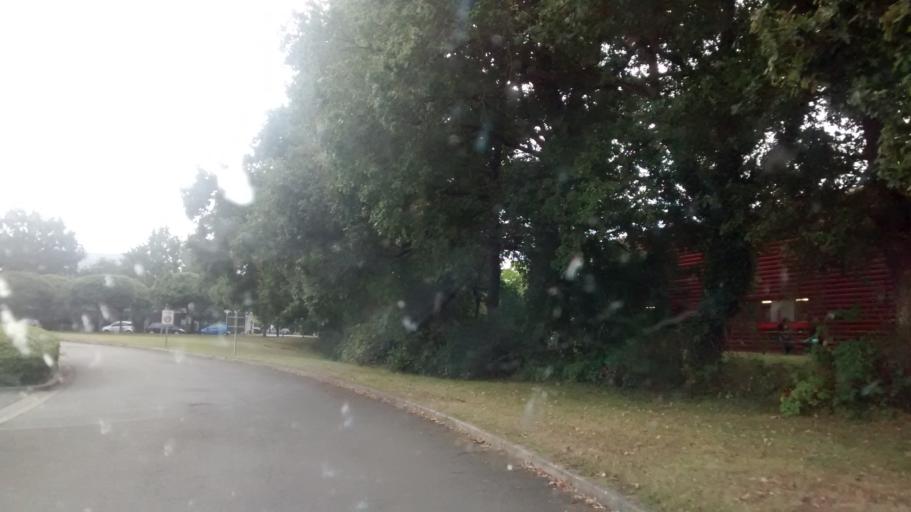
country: FR
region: Brittany
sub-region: Departement d'Ille-et-Vilaine
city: Saint-Jacques-de-la-Lande
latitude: 48.0509
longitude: -1.7425
